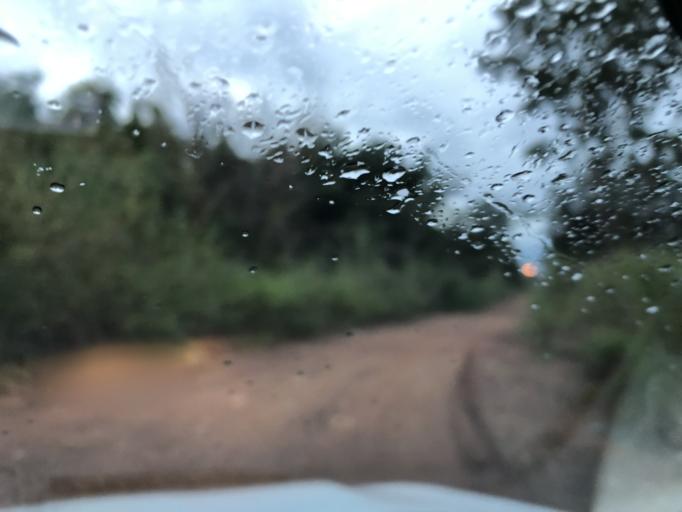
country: BR
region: Goias
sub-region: Luziania
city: Luziania
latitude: -16.1182
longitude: -47.9856
